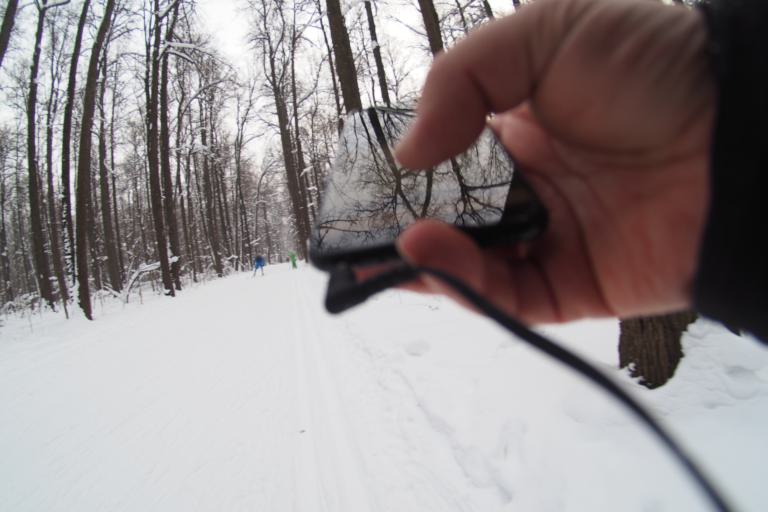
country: RU
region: Moskovskaya
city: Izmaylovo
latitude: 55.7701
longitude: 37.7773
